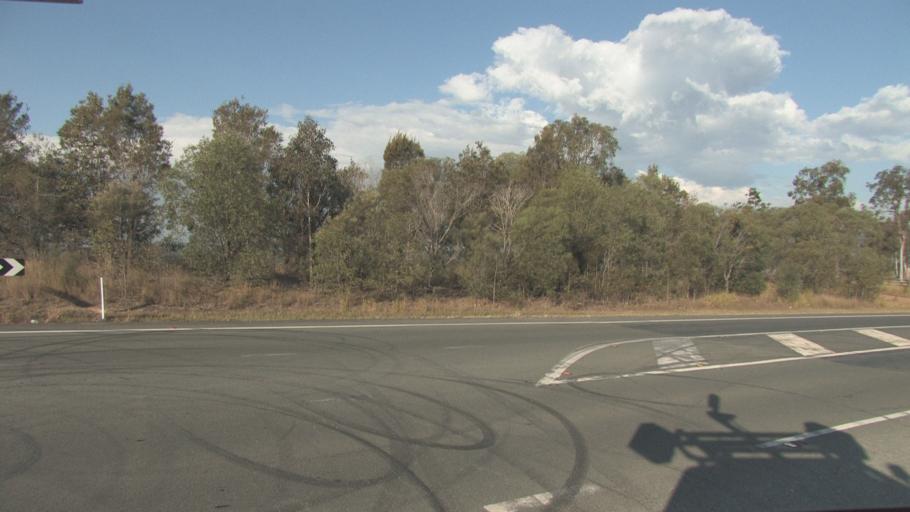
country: AU
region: Queensland
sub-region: Logan
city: Cedar Vale
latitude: -27.8498
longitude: 153.1212
